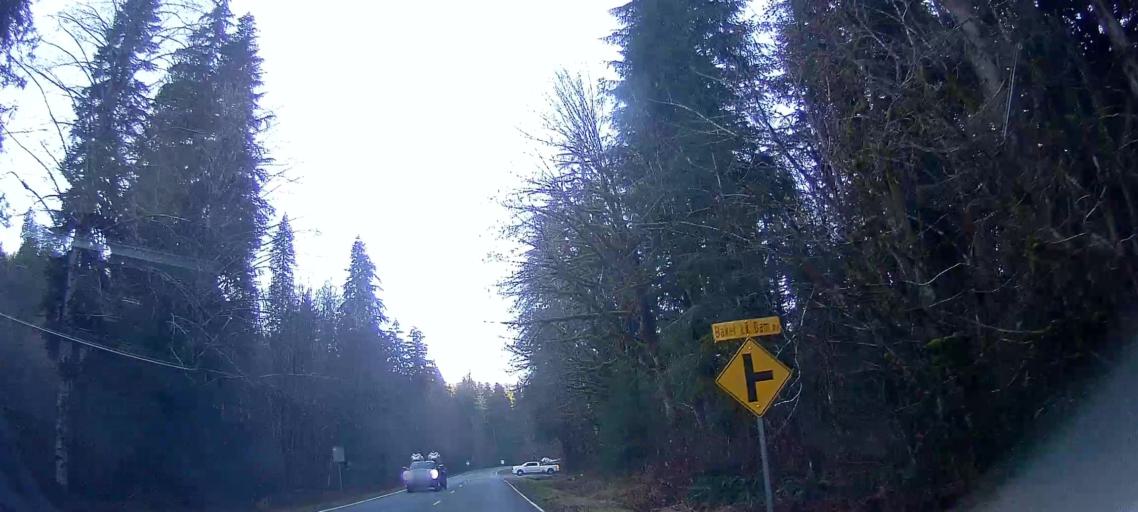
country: US
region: Washington
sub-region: Snohomish County
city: Darrington
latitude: 48.6625
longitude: -121.7165
